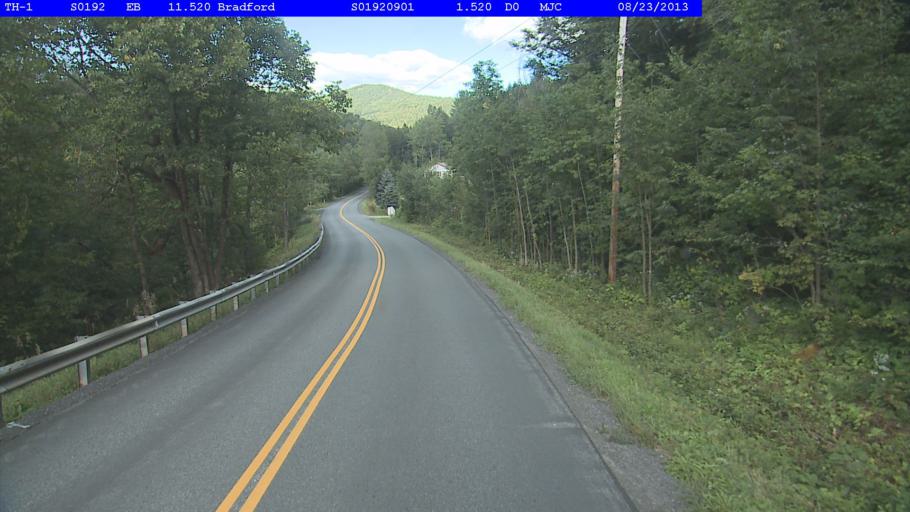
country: US
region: New Hampshire
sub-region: Grafton County
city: Haverhill
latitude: 44.0283
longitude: -72.1960
